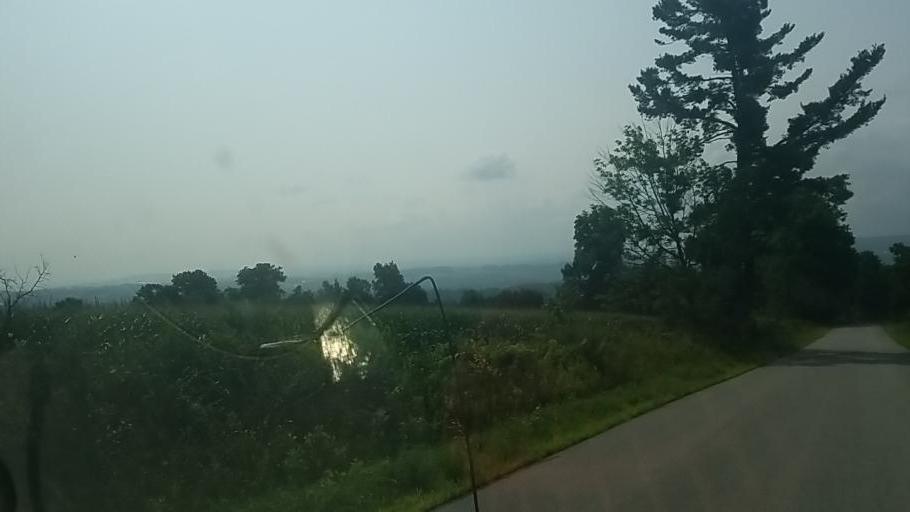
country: US
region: New York
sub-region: Montgomery County
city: Fonda
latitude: 42.9443
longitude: -74.4506
